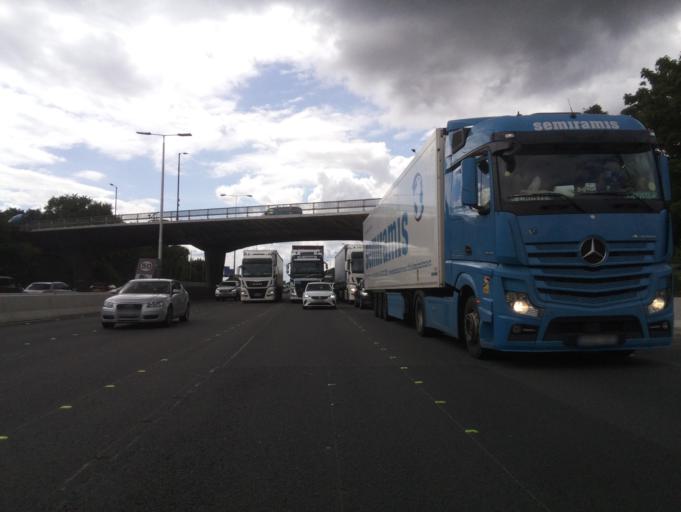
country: GB
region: England
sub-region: Surrey
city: Colnbrook
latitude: 51.4936
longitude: -0.5317
